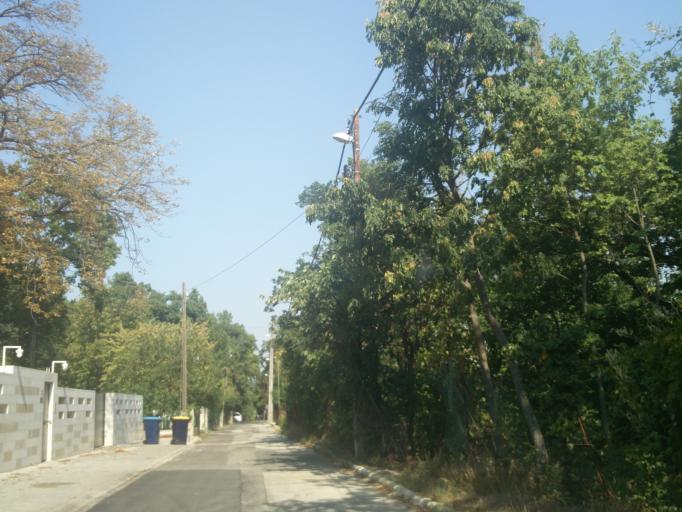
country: HU
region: Budapest
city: Budapest XII. keruelet
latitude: 47.5038
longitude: 18.9954
